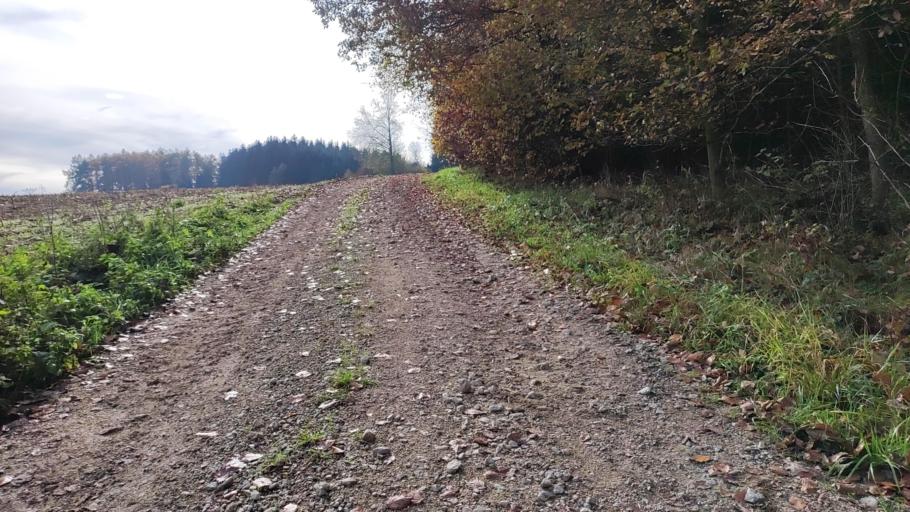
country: DE
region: Bavaria
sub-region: Swabia
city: Langenneufnach
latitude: 48.2881
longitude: 10.6011
